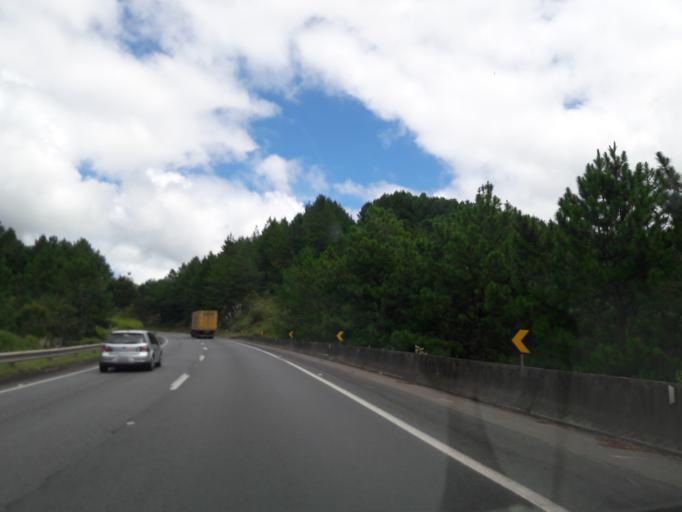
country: BR
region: Parana
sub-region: Campina Grande Do Sul
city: Campina Grande do Sul
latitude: -25.1060
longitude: -48.8474
